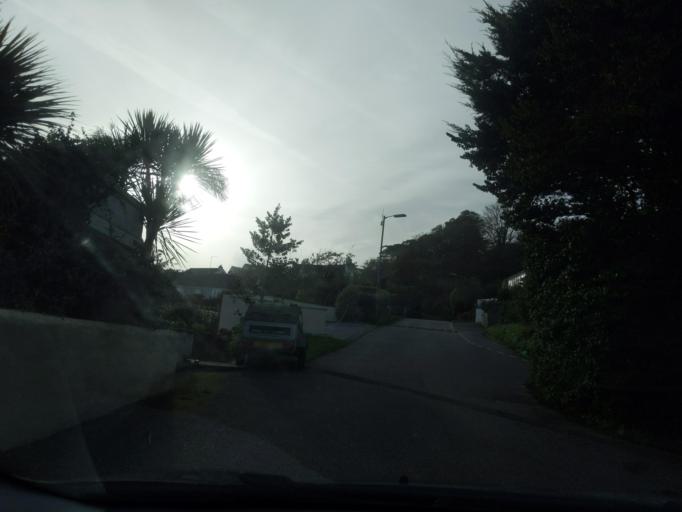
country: GB
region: England
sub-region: Cornwall
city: Looe
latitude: 50.3588
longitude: -4.4439
